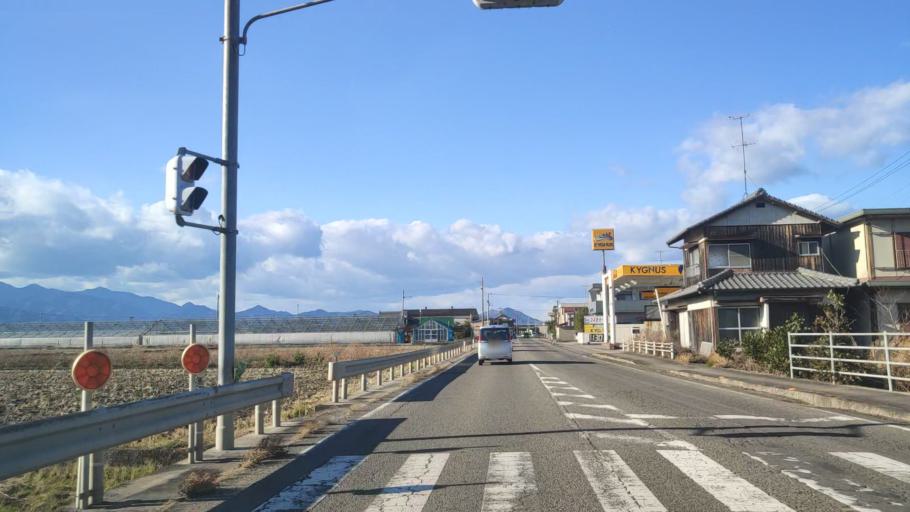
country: JP
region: Ehime
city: Saijo
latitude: 33.9143
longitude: 133.1070
